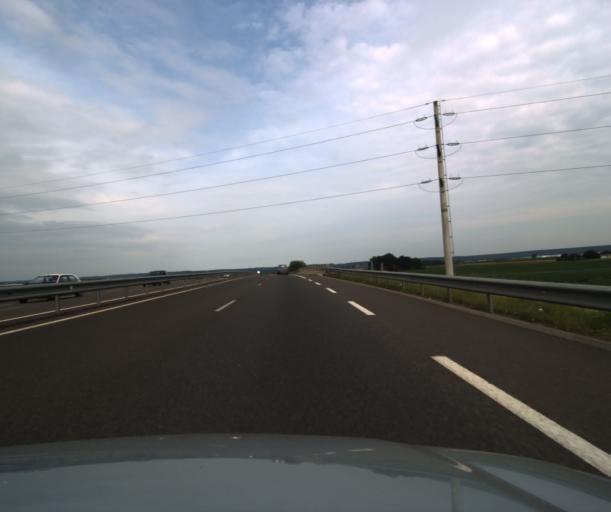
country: FR
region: Midi-Pyrenees
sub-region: Departement des Hautes-Pyrenees
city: Juillan
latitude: 43.2231
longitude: 0.0368
